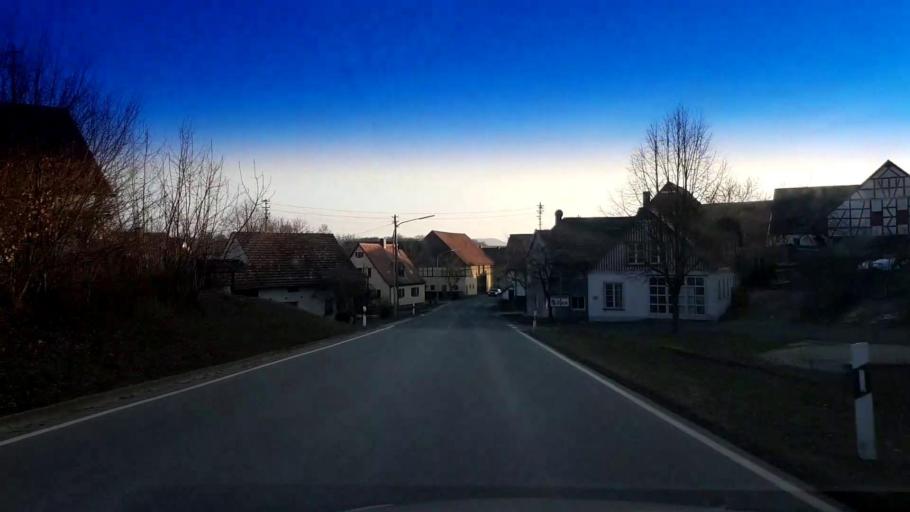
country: DE
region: Bavaria
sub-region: Upper Franconia
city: Schesslitz
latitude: 50.0057
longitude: 11.0160
